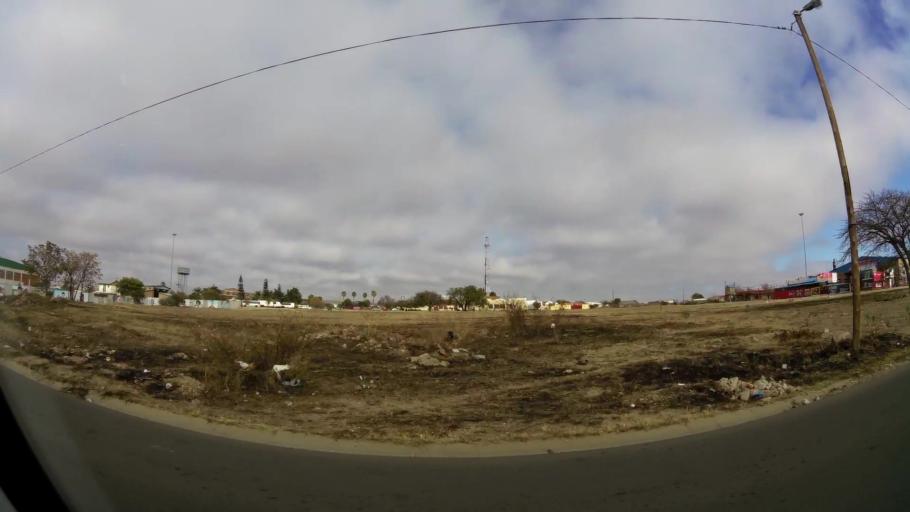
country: ZA
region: Limpopo
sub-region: Capricorn District Municipality
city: Polokwane
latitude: -23.8519
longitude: 29.3843
